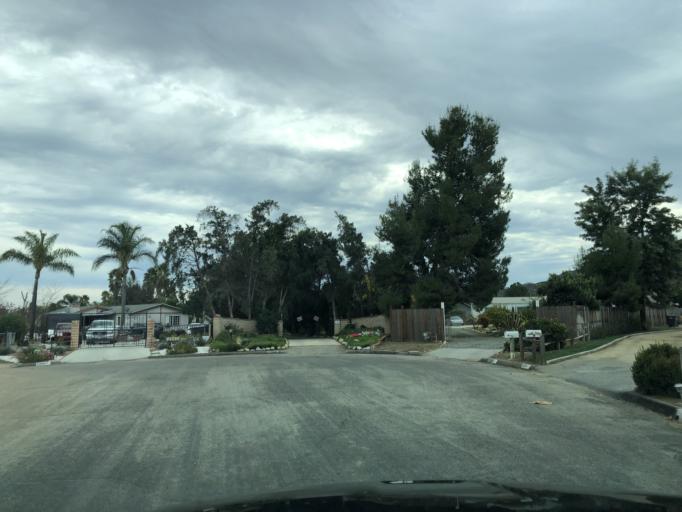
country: US
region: California
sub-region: Riverside County
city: Wildomar
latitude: 33.6045
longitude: -117.2839
